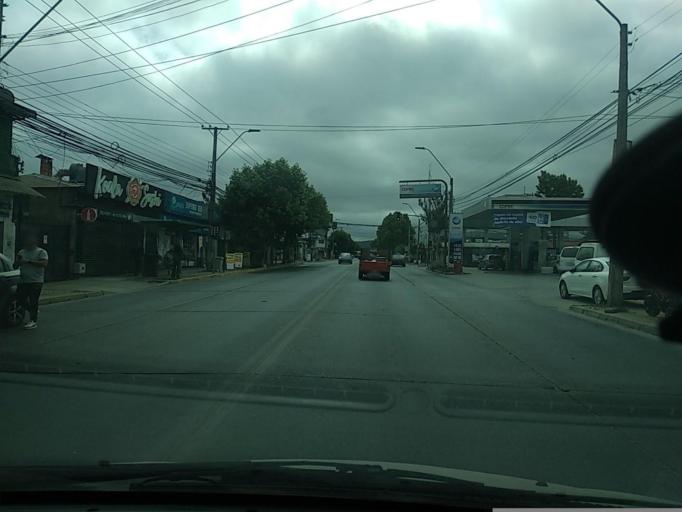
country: CL
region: Valparaiso
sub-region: Provincia de Marga Marga
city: Villa Alemana
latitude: -33.0444
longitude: -71.3818
